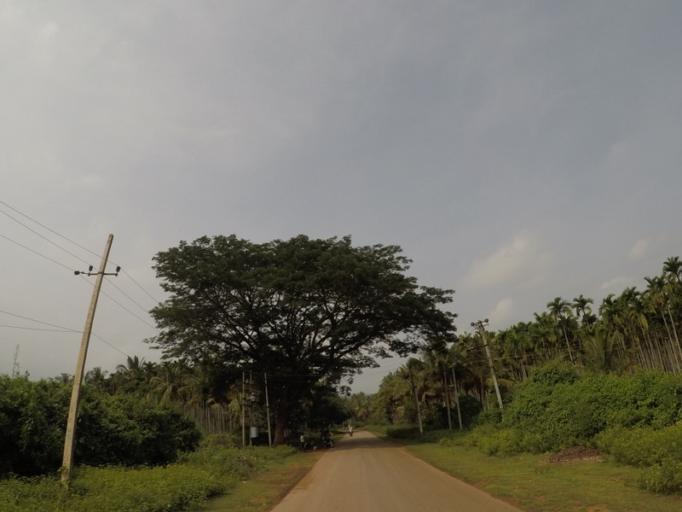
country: IN
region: Karnataka
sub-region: Chikmagalur
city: Tarikere
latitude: 13.5928
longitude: 75.8365
